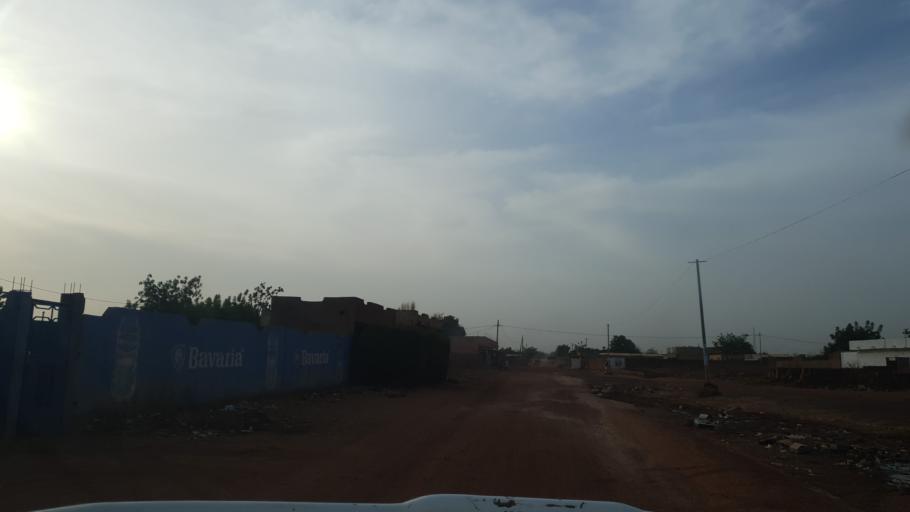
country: ML
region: Segou
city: Baroueli
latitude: 12.7860
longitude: -6.9459
